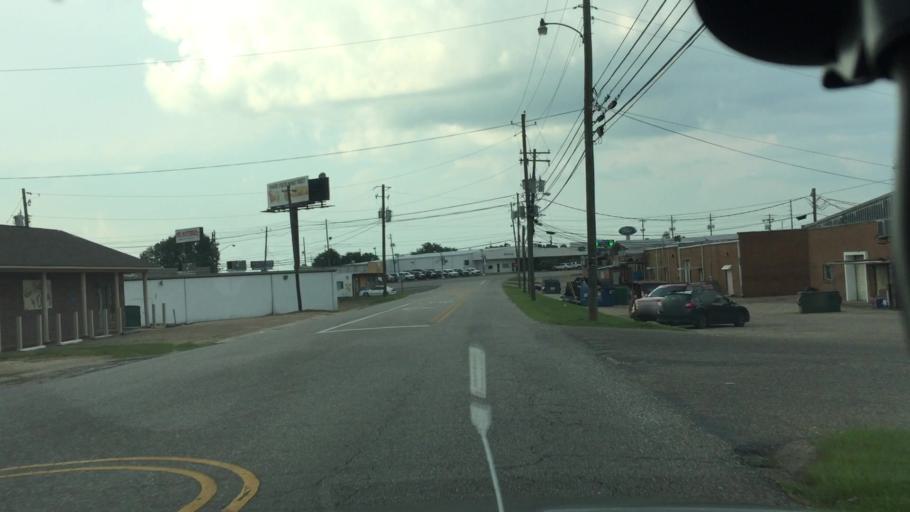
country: US
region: Alabama
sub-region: Coffee County
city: Enterprise
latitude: 31.3211
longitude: -85.8332
